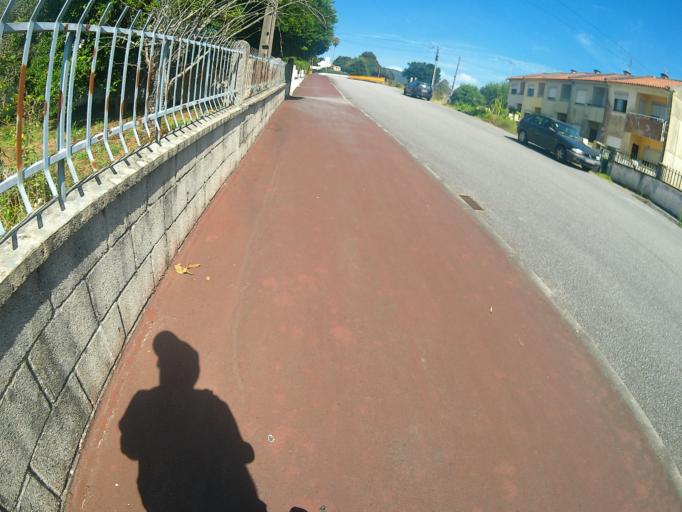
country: PT
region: Viana do Castelo
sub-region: Valenca
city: Valenca
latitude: 42.0254
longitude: -8.6513
